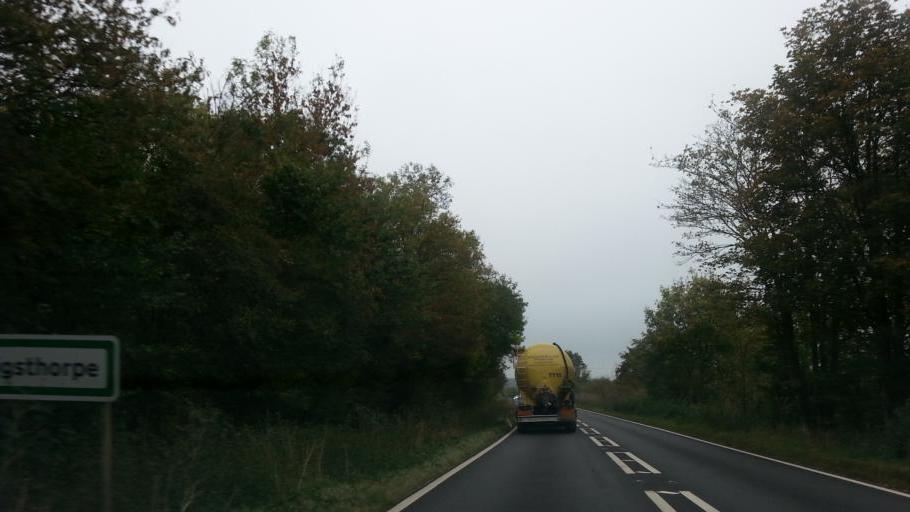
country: GB
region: England
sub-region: Northamptonshire
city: Oundle
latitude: 52.4389
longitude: -0.4743
